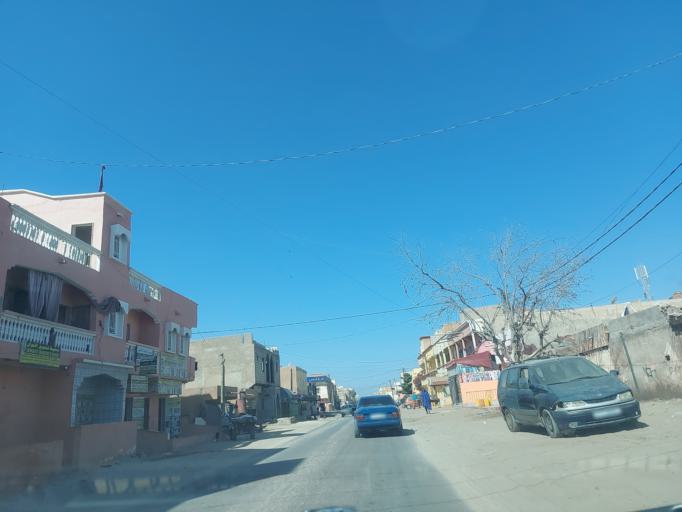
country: MR
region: Nouakchott
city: Nouakchott
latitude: 18.0754
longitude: -15.9974
